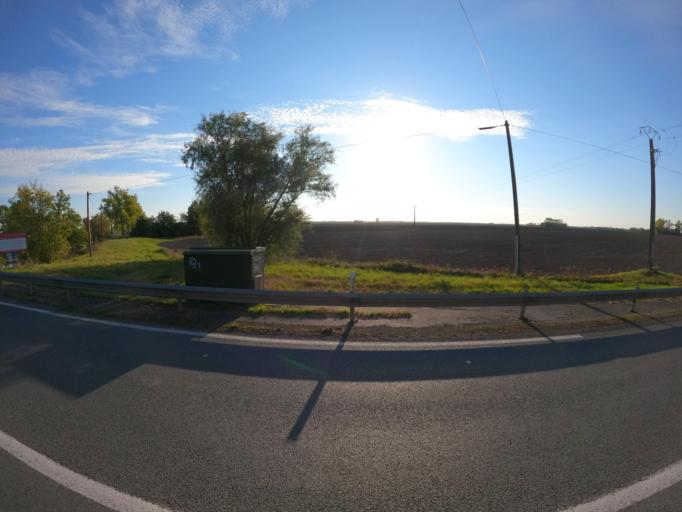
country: FR
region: Pays de la Loire
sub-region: Departement de la Vendee
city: Chaille-les-Marais
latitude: 46.4095
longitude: -1.0376
